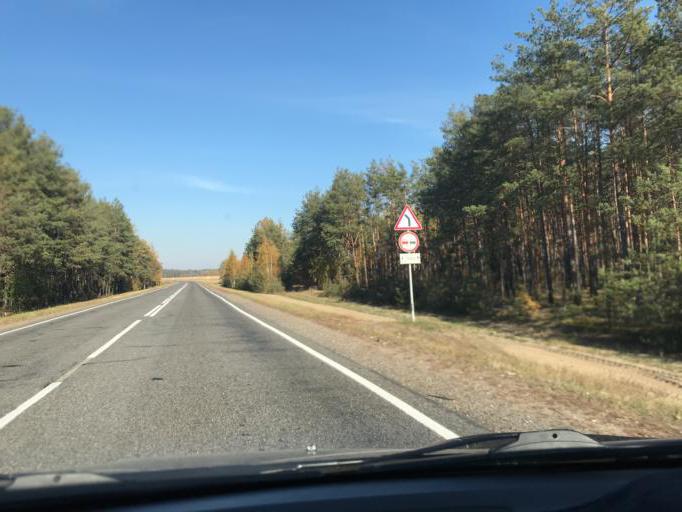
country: BY
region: Gomel
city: Parychy
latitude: 52.7378
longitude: 29.3949
